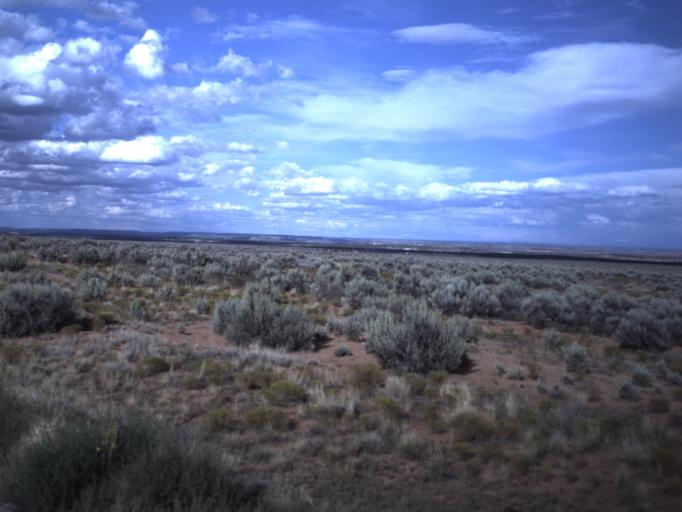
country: US
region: Utah
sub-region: San Juan County
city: Blanding
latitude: 37.3820
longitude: -109.3411
